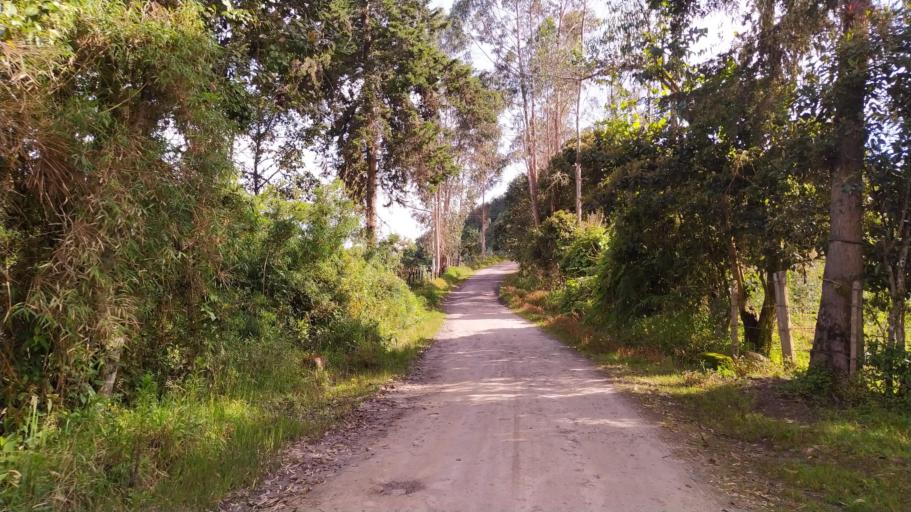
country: CO
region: Cundinamarca
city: Tenza
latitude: 5.0888
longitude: -73.4786
